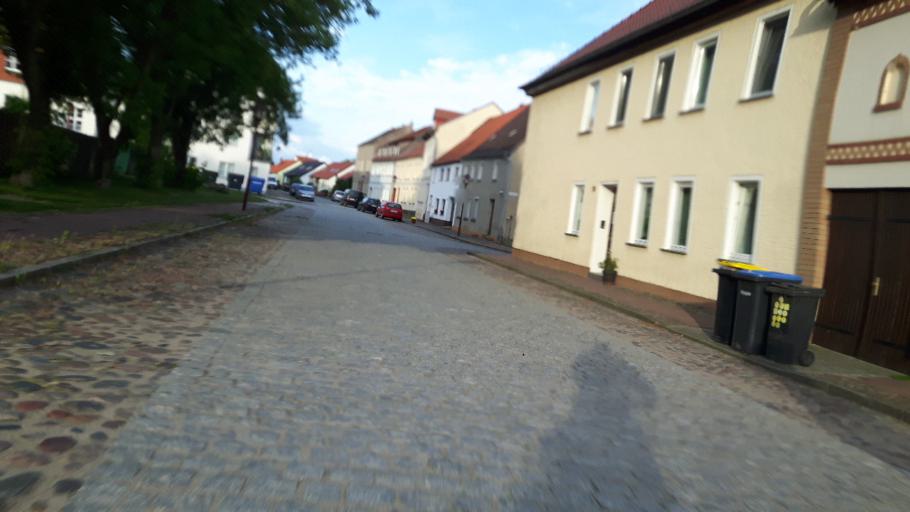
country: DE
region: Brandenburg
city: Gartz
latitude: 53.2070
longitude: 14.3923
